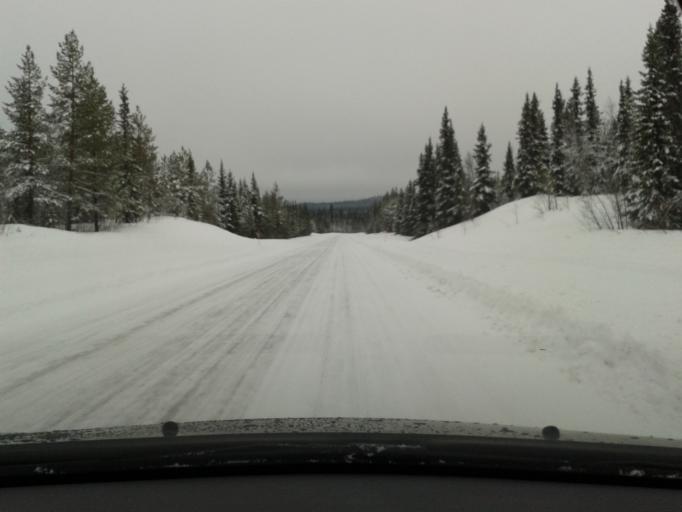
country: SE
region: Vaesterbotten
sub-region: Vilhelmina Kommun
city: Sjoberg
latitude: 65.1385
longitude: 15.8741
